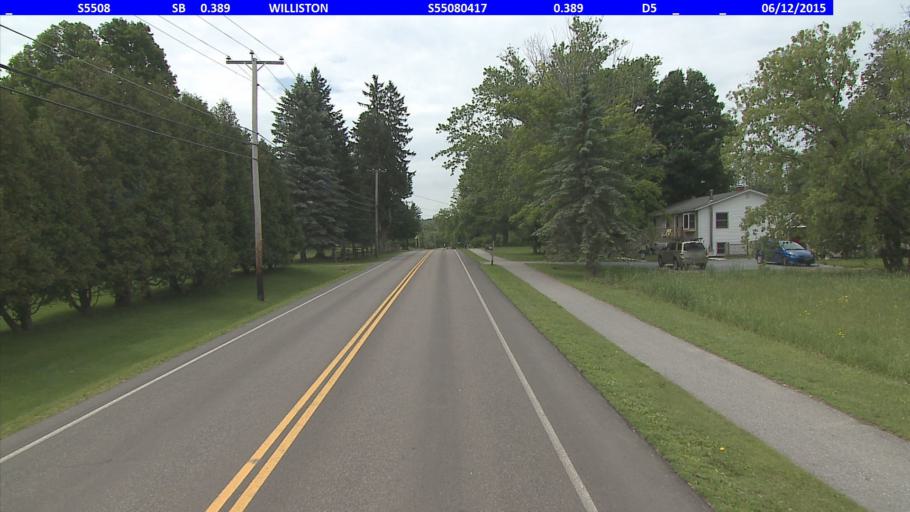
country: US
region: Vermont
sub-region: Chittenden County
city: Williston
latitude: 44.4424
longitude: -73.0647
